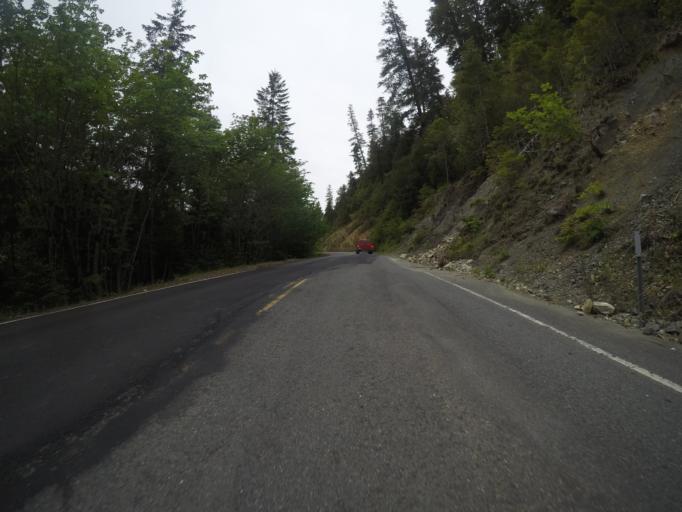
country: US
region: California
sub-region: Del Norte County
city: Bertsch-Oceanview
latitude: 41.7220
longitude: -123.9503
